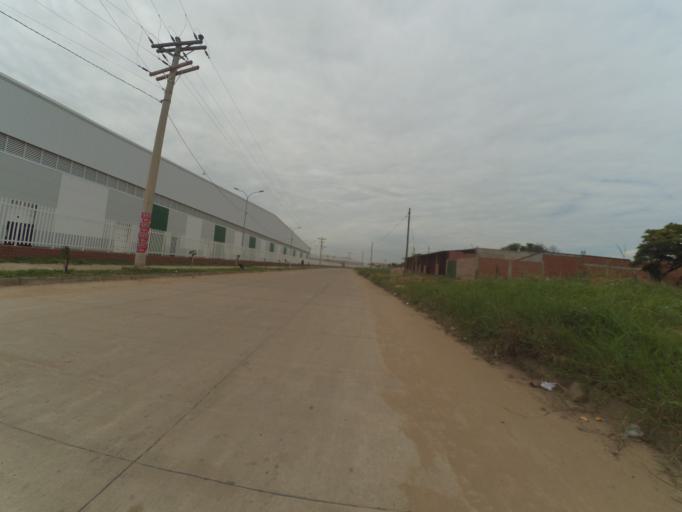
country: BO
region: Santa Cruz
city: Santa Cruz de la Sierra
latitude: -17.8342
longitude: -63.2165
